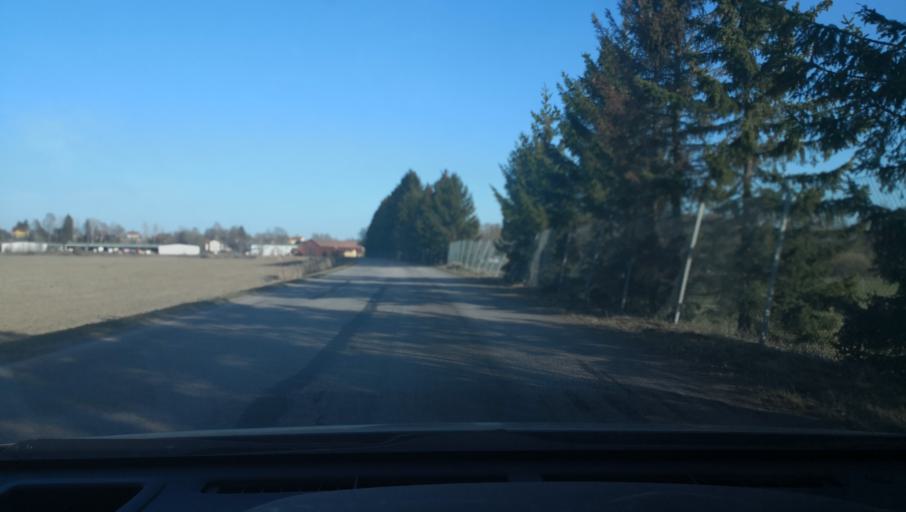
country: SE
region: Uppsala
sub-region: Heby Kommun
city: Heby
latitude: 59.9464
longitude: 16.8474
